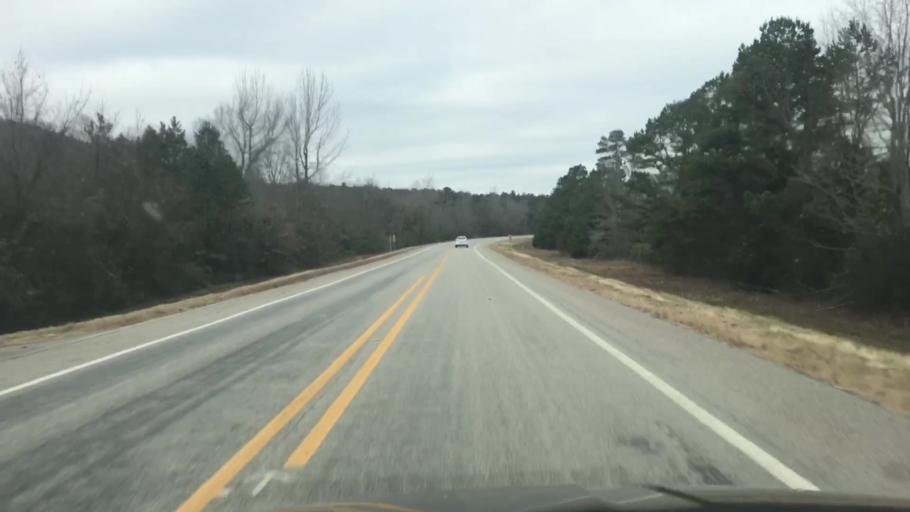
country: US
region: Arkansas
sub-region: Scott County
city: Waldron
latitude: 34.7037
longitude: -93.9242
